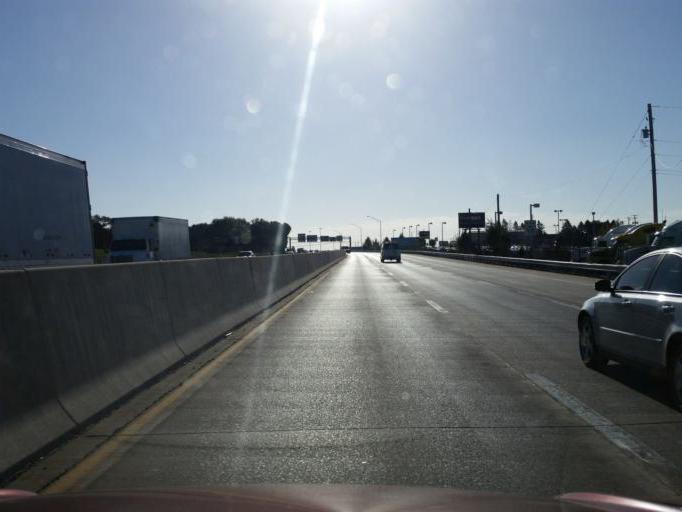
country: US
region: Pennsylvania
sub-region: Lancaster County
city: East Petersburg
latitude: 40.0740
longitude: -76.3326
